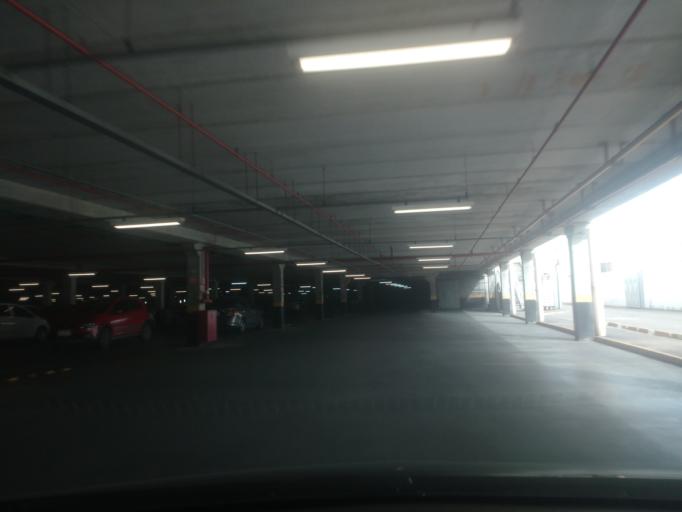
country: BR
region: Alagoas
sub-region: Maceio
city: Maceio
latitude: -9.6503
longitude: -35.7180
